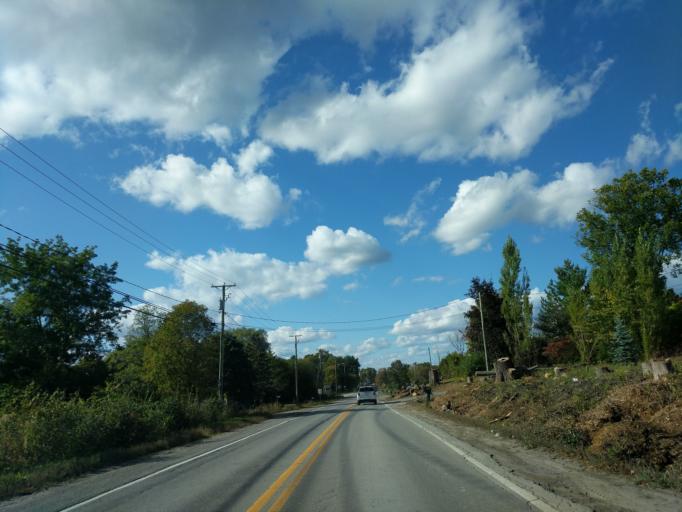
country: CA
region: Ontario
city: Bells Corners
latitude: 45.4410
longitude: -75.9161
